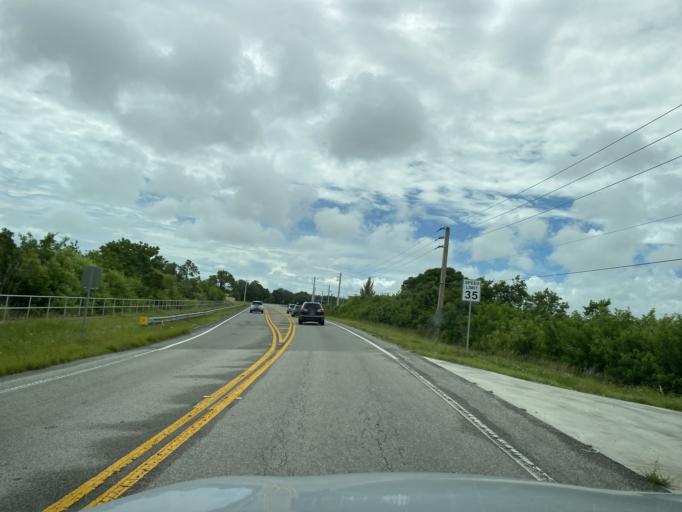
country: US
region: Florida
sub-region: Brevard County
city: West Melbourne
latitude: 28.0402
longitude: -80.6536
